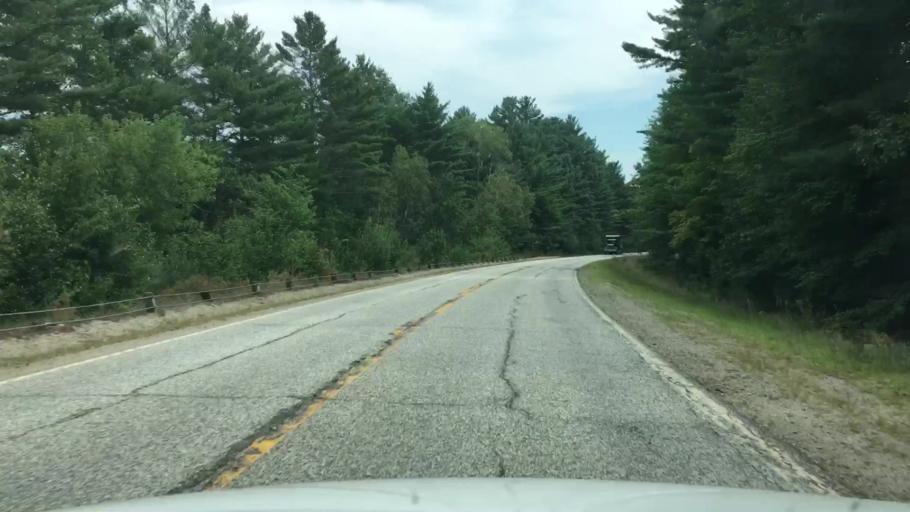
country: US
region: Maine
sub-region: Oxford County
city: Rumford
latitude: 44.6135
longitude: -70.7382
